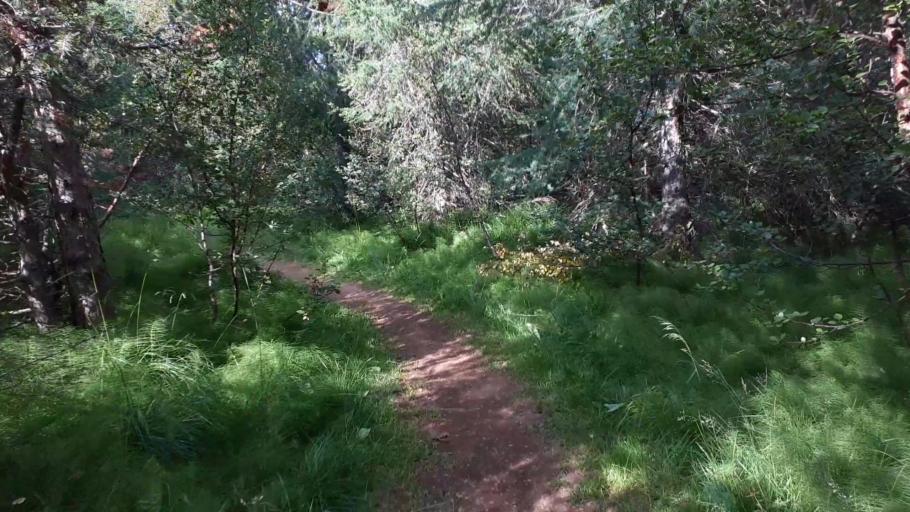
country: IS
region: Northeast
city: Akureyri
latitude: 65.6396
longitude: -18.0943
